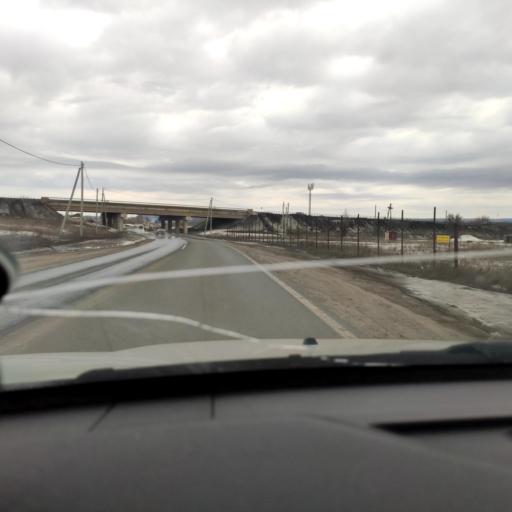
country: RU
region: Samara
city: Kurumoch
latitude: 53.4978
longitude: 50.0574
